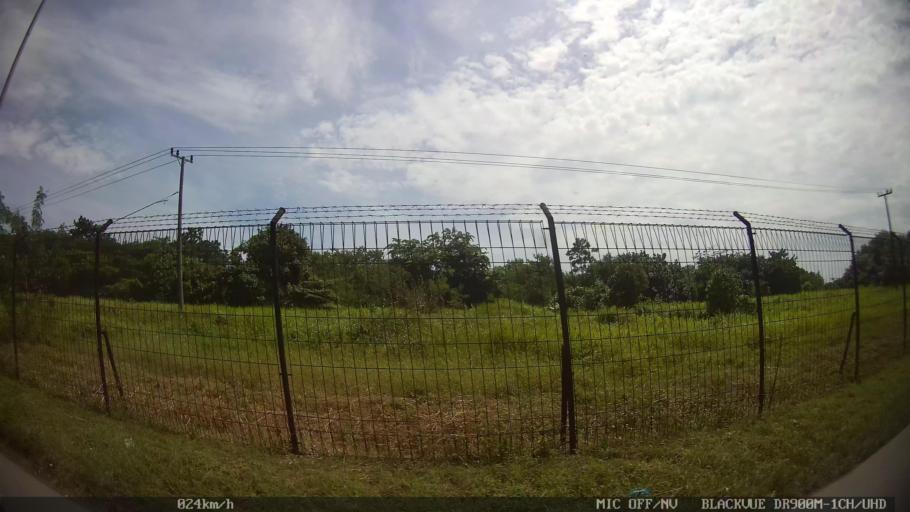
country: ID
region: North Sumatra
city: Percut
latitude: 3.6048
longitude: 98.8601
